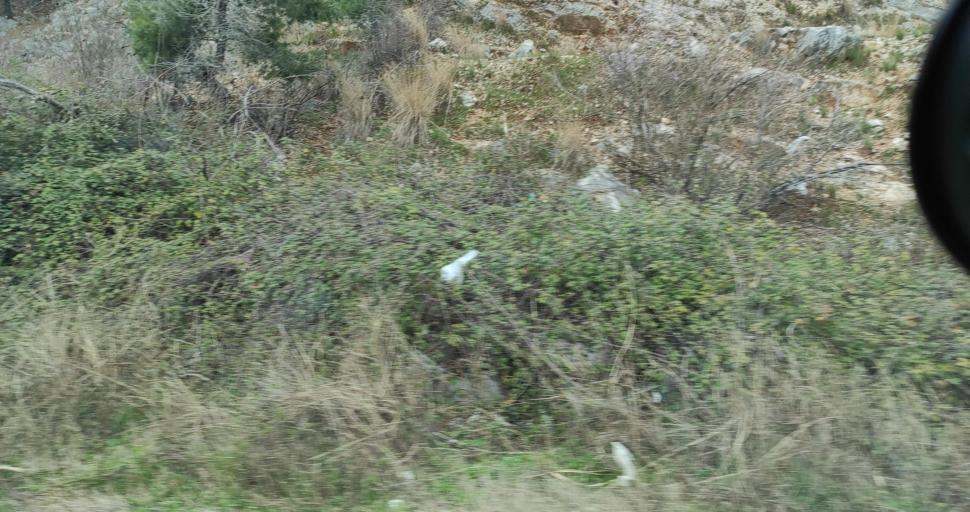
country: AL
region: Lezhe
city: Lezhe
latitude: 41.7898
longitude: 19.6258
